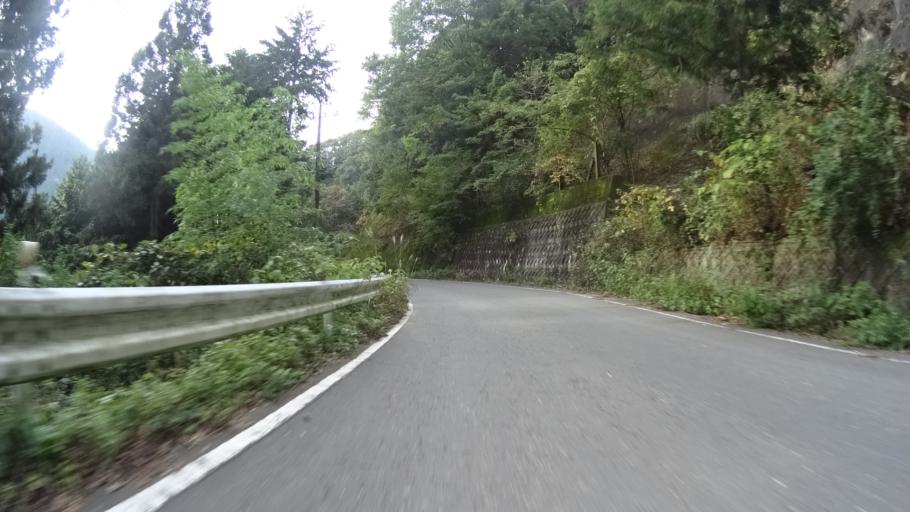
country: JP
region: Yamanashi
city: Uenohara
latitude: 35.6824
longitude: 139.0986
